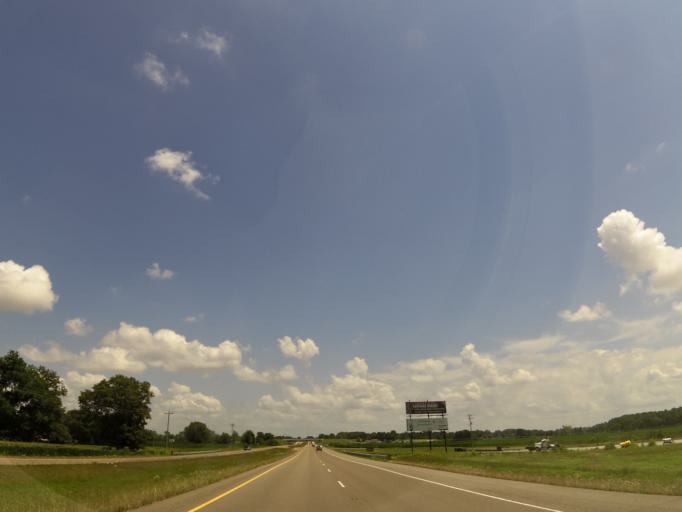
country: US
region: Tennessee
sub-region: Crockett County
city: Alamo
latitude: 35.8248
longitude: -89.1734
